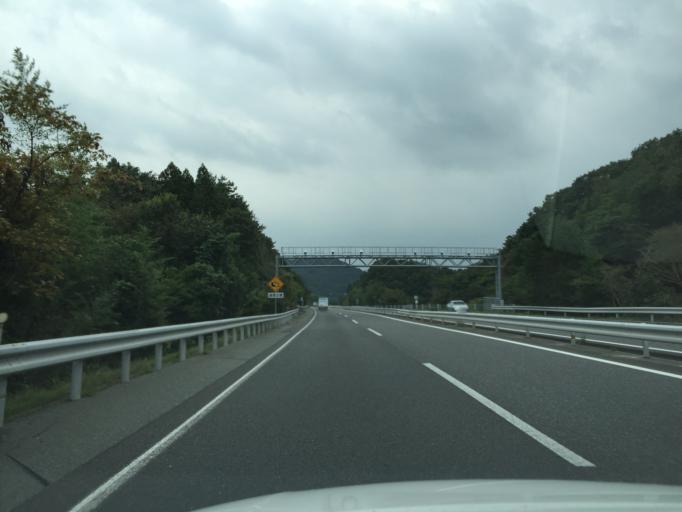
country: JP
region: Fukushima
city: Iwaki
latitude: 37.0570
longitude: 140.8000
